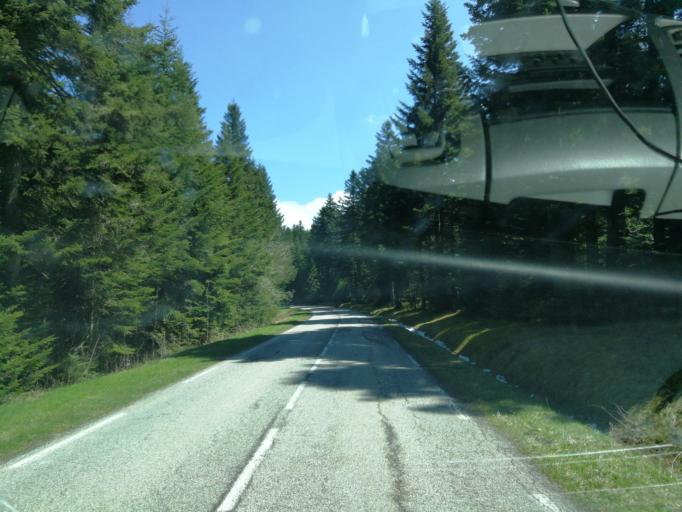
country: FR
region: Rhone-Alpes
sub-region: Departement de l'Ardeche
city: Saint-Agreve
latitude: 45.1068
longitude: 4.4025
